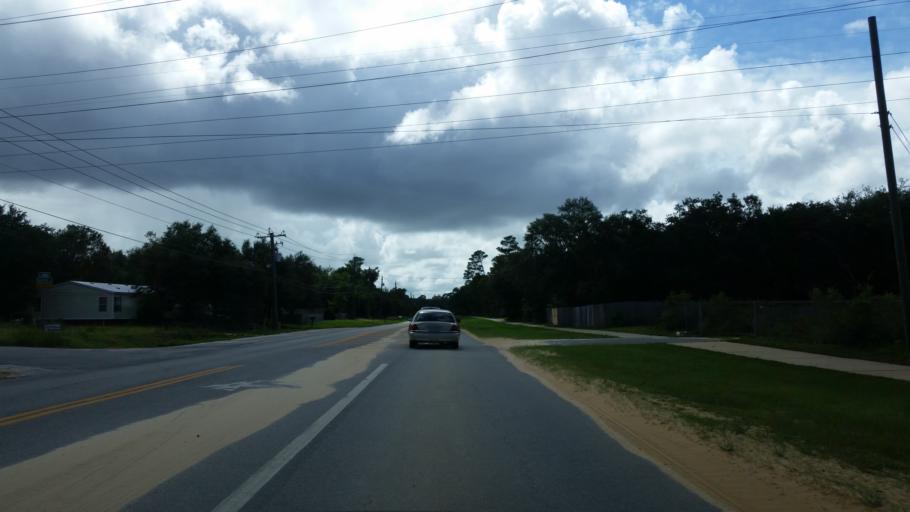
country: US
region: Florida
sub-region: Santa Rosa County
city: Holley
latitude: 30.4461
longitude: -86.9370
